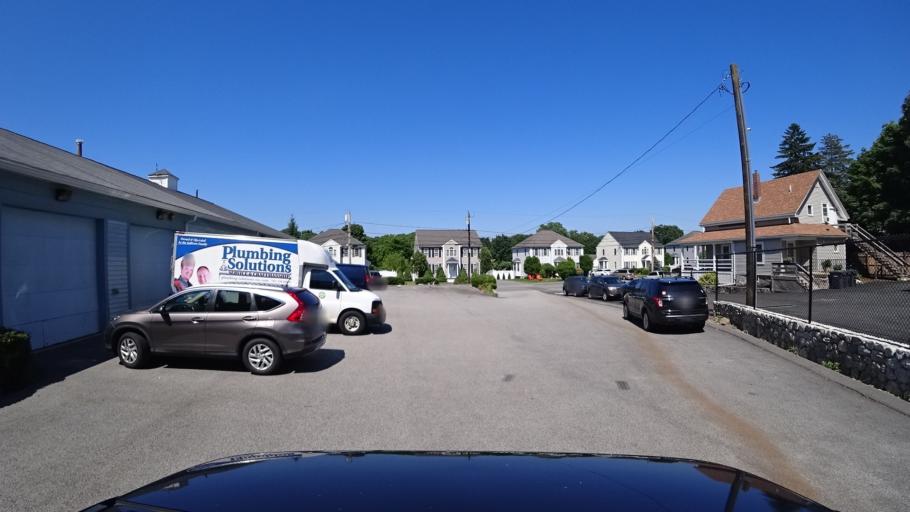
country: US
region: Massachusetts
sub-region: Norfolk County
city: Dedham
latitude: 42.2434
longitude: -71.1543
